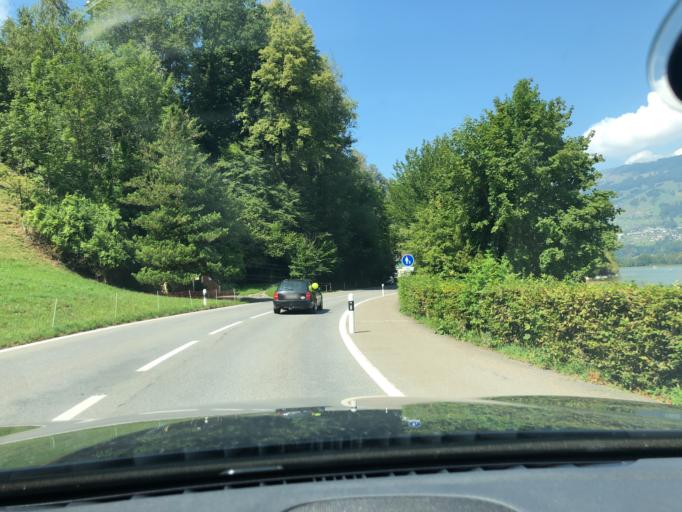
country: CH
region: Schwyz
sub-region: Bezirk Schwyz
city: Steinen
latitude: 47.0267
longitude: 8.6057
